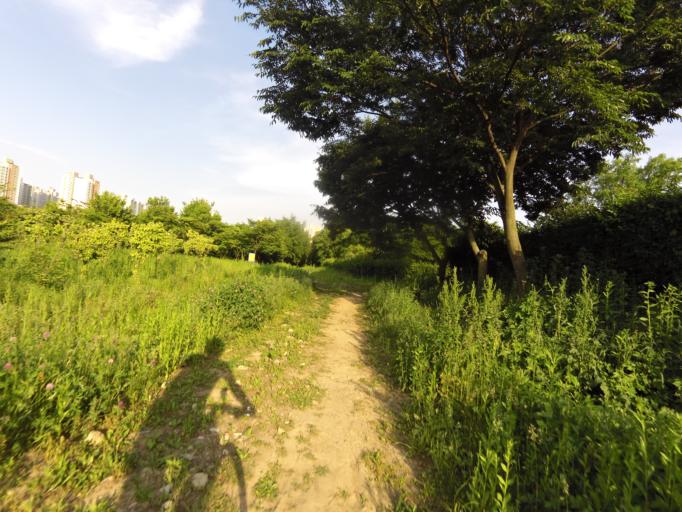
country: KR
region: Gyeongsangbuk-do
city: Gyeongsan-si
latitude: 35.8374
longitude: 128.7624
